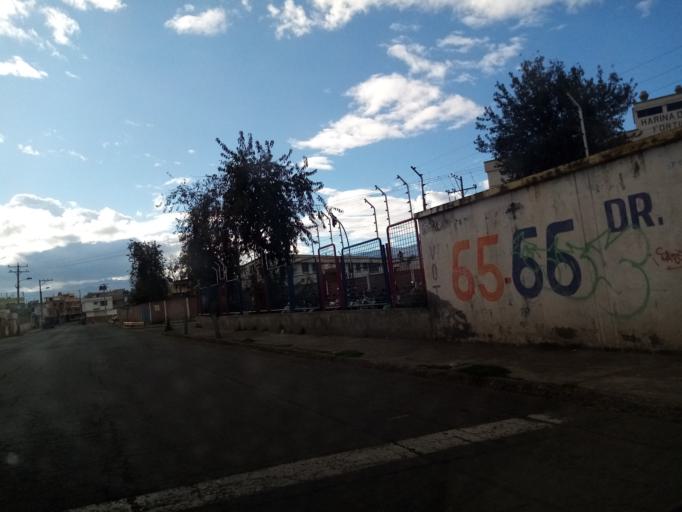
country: EC
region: Chimborazo
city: Riobamba
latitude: -1.6846
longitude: -78.6329
